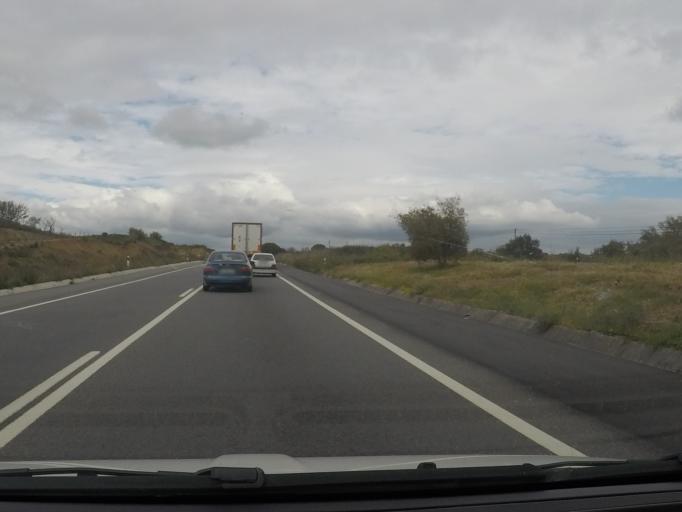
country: PT
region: Setubal
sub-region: Santiago do Cacem
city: Santiago do Cacem
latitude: 38.0687
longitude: -8.6838
